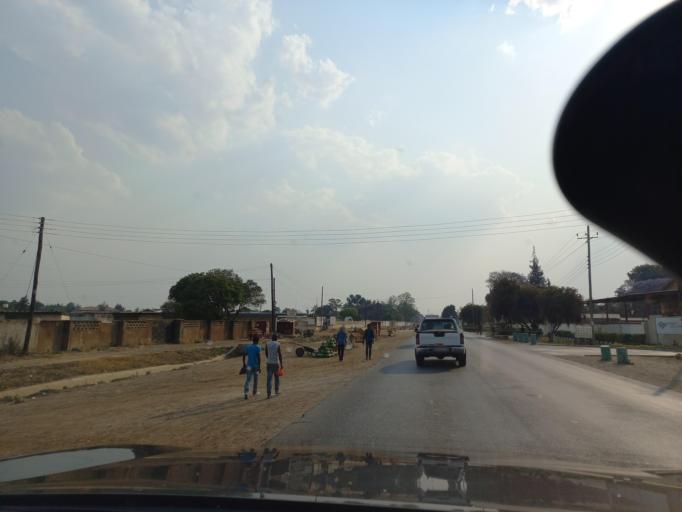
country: ZM
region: Lusaka
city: Lusaka
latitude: -15.4558
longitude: 28.2645
